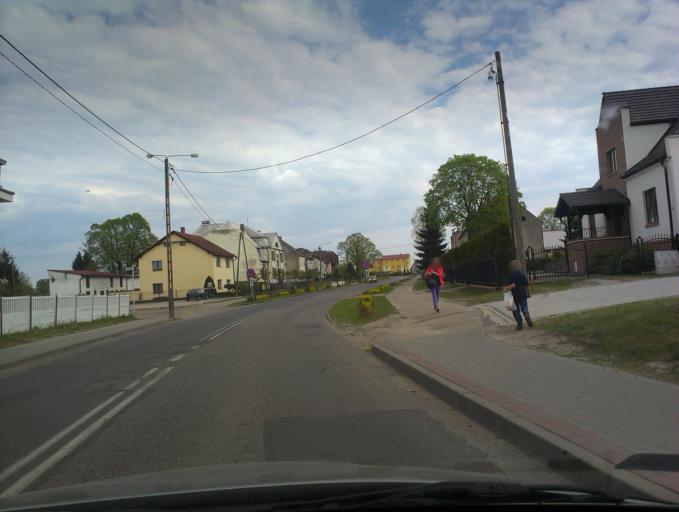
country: PL
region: Pomeranian Voivodeship
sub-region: Powiat czluchowski
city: Czarne
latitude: 53.6825
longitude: 16.9454
